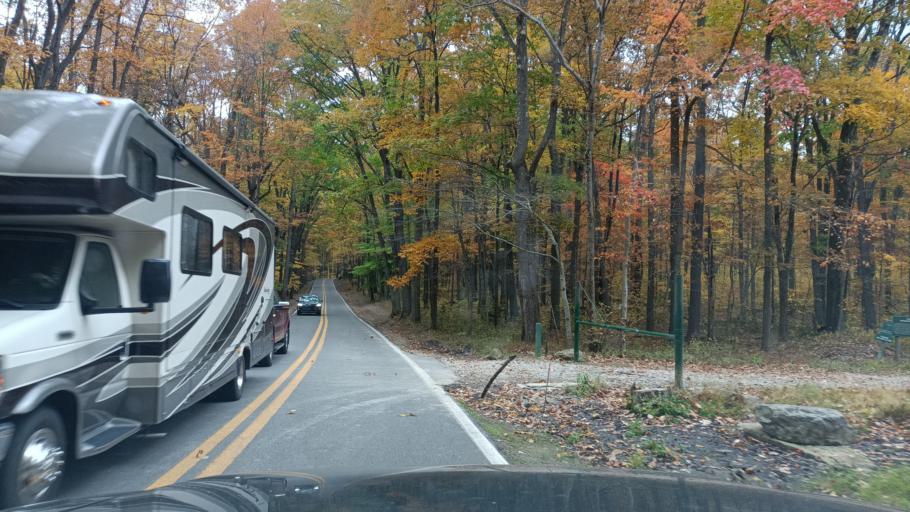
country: US
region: West Virginia
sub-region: Monongalia County
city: Cheat Lake
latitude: 39.6366
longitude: -79.8015
